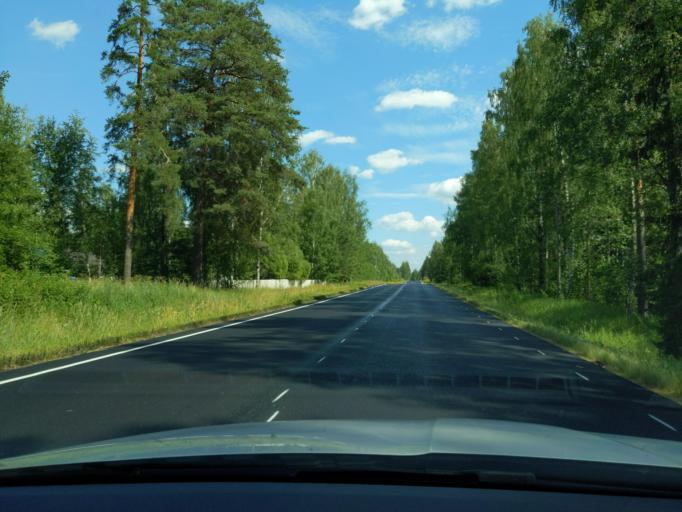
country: FI
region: Paijanne Tavastia
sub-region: Lahti
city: Nastola
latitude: 61.0893
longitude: 25.8703
